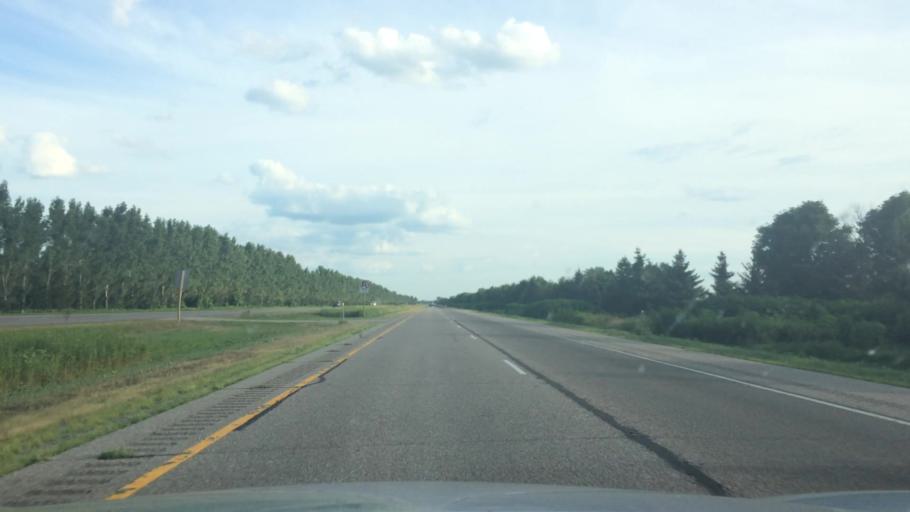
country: US
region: Wisconsin
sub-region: Portage County
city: Plover
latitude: 44.3568
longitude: -89.5212
